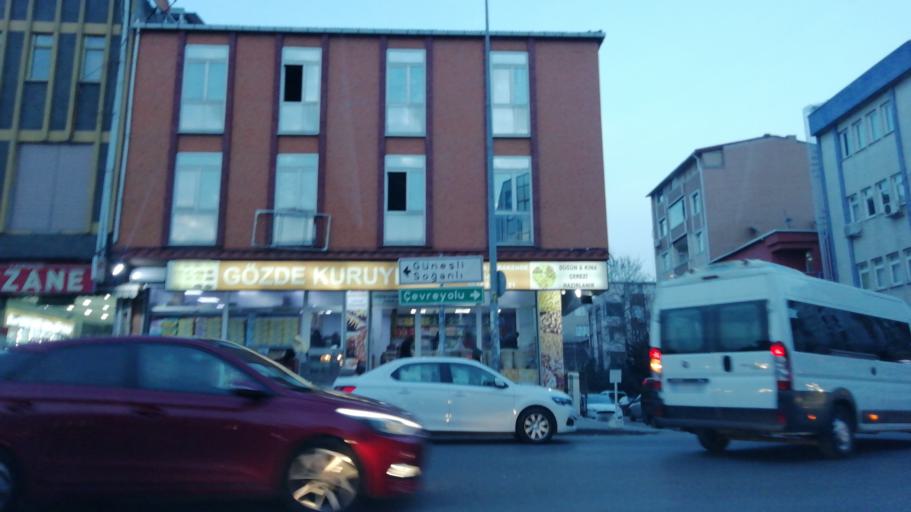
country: TR
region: Istanbul
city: Bahcelievler
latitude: 41.0110
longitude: 28.8287
